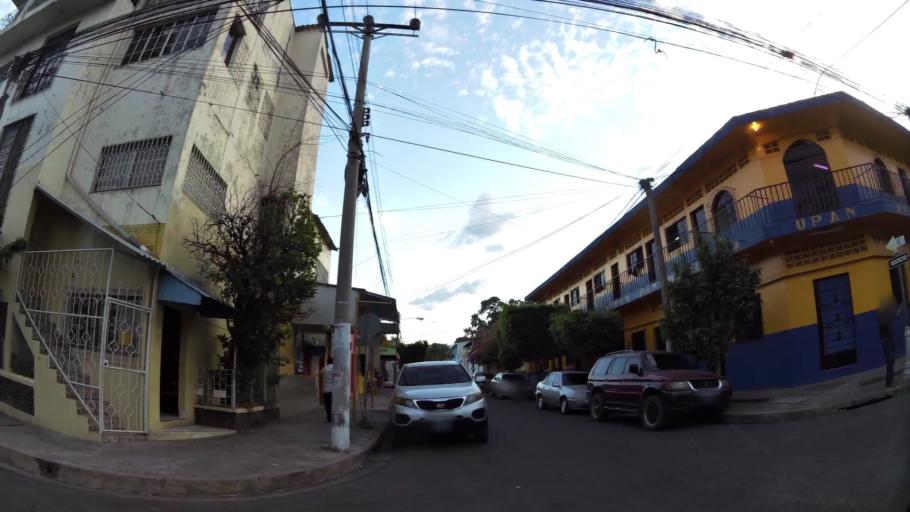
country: SV
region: San Vicente
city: San Vicente
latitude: 13.6461
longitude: -88.7854
